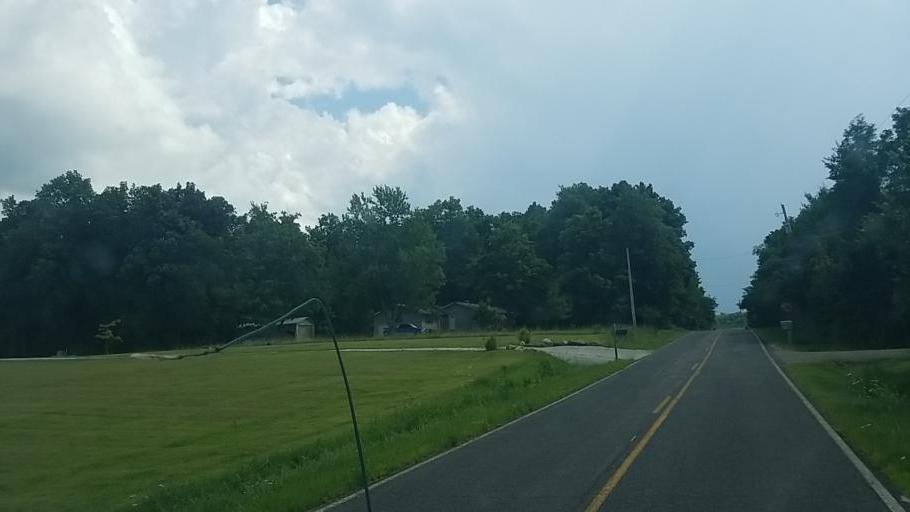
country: US
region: Ohio
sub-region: Medina County
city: Medina
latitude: 41.1384
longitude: -81.9545
